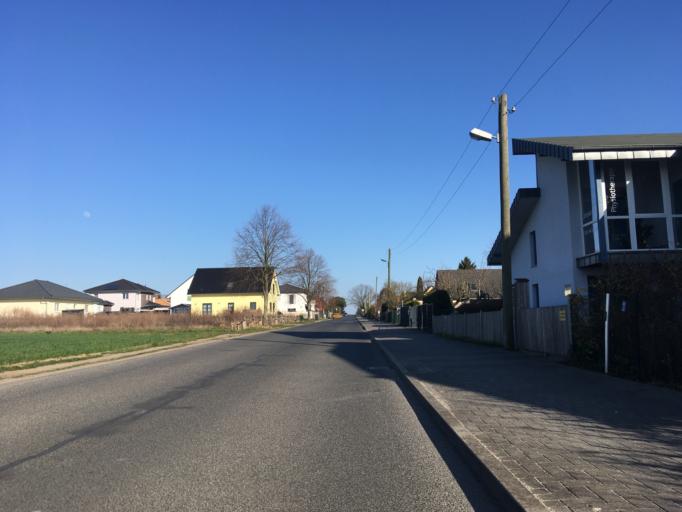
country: DE
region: Berlin
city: Falkenberg
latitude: 52.6017
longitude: 13.5509
